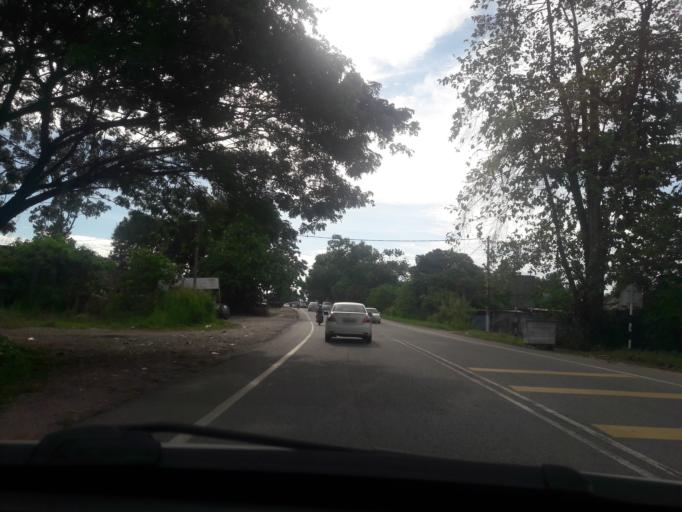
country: MY
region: Kedah
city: Sungai Petani
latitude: 5.6354
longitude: 100.5130
